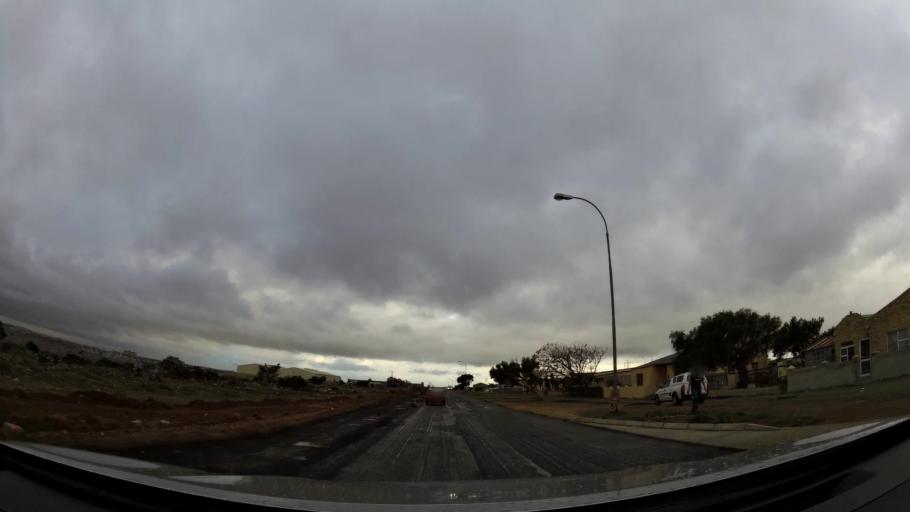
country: ZA
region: Eastern Cape
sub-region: Nelson Mandela Bay Metropolitan Municipality
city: Port Elizabeth
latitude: -33.8953
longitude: 25.5428
